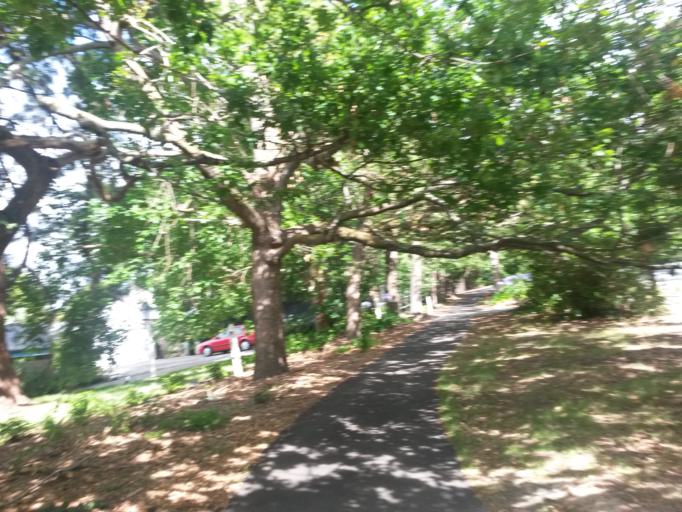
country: AU
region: South Australia
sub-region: Adelaide Hills
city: Heathfield
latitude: -35.0049
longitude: 138.7133
